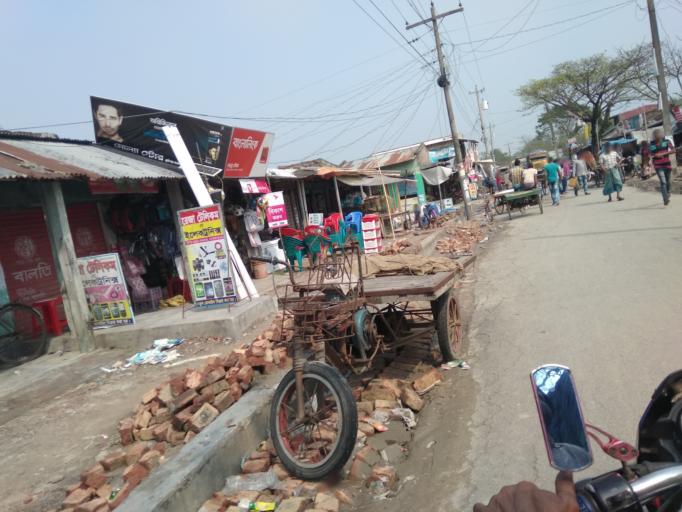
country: IN
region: West Bengal
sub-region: North 24 Parganas
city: Gosaba
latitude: 22.2698
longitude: 89.1959
